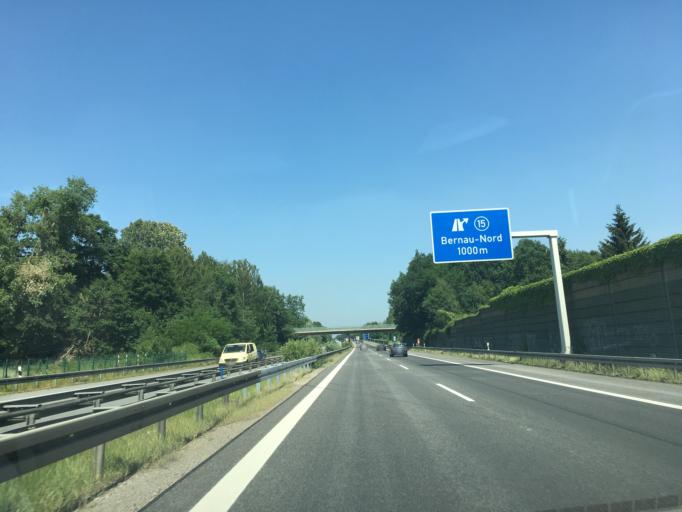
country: DE
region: Brandenburg
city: Bernau bei Berlin
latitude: 52.6797
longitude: 13.5639
